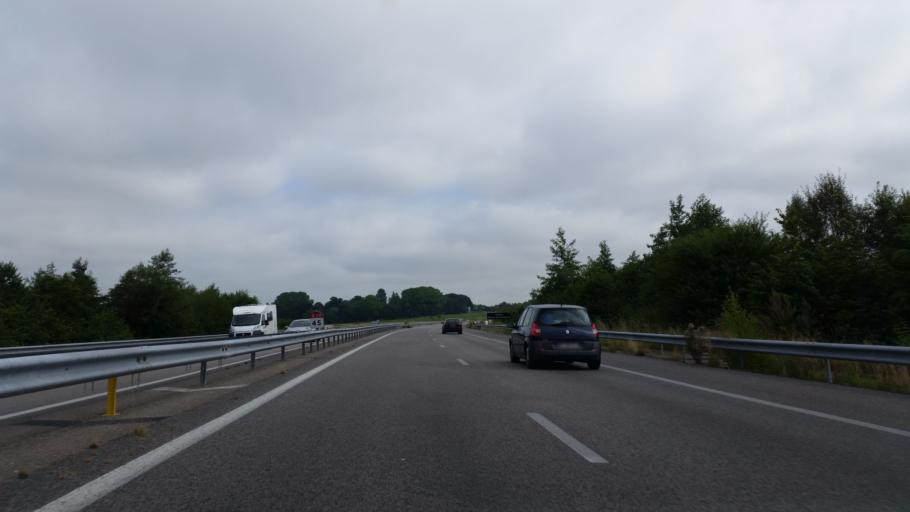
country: FR
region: Haute-Normandie
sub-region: Departement de la Seine-Maritime
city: Nointot
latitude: 49.5945
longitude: 0.4528
